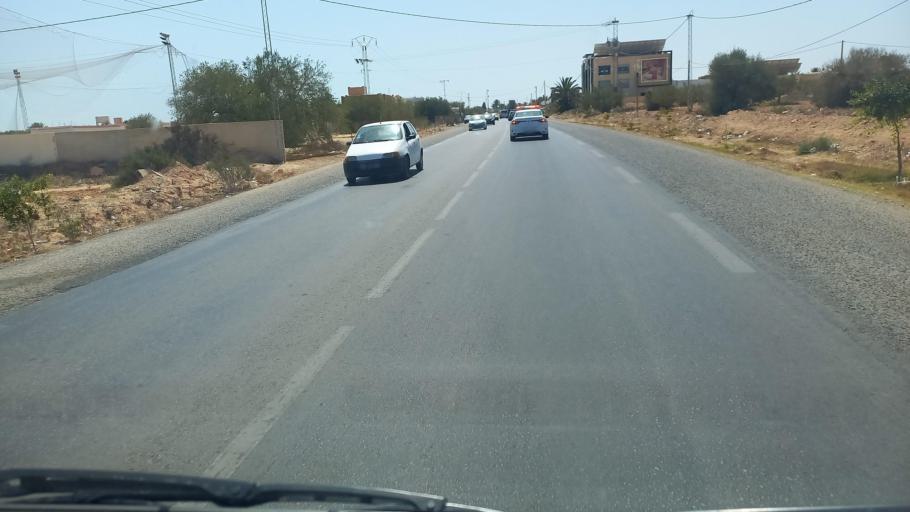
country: TN
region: Madanin
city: Houmt Souk
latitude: 33.8142
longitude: 10.8758
